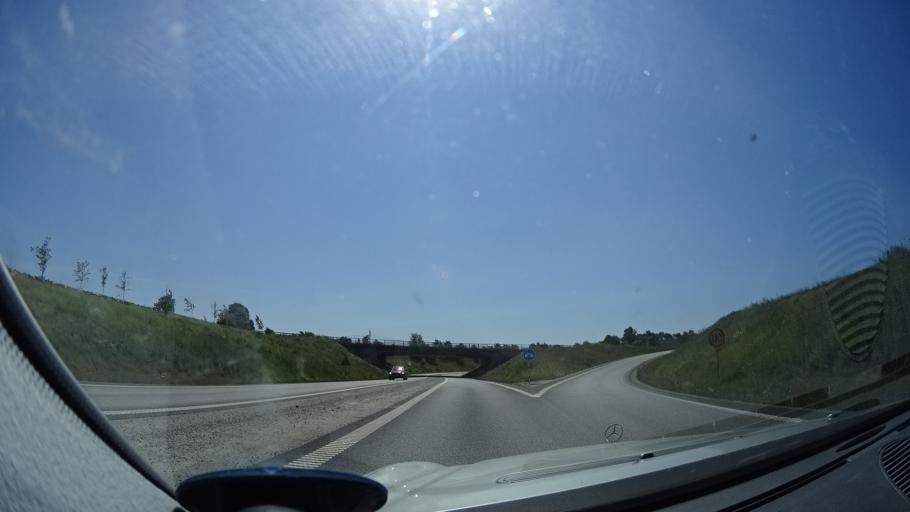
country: SE
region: Skane
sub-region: Hoors Kommun
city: Loberod
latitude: 55.8103
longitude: 13.4783
